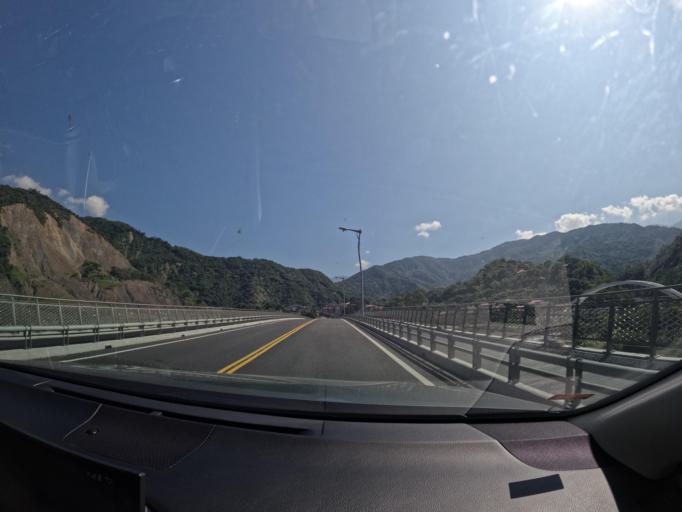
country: TW
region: Taiwan
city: Yujing
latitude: 23.1063
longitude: 120.6961
